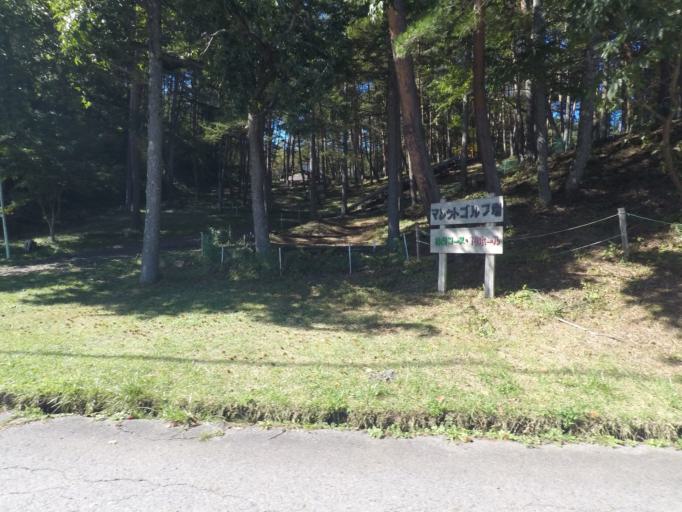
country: JP
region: Nagano
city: Ina
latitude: 35.9684
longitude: 137.7464
